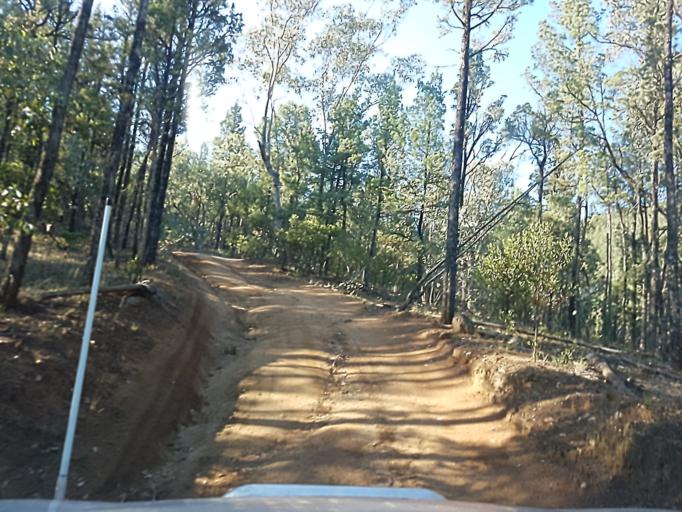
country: AU
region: New South Wales
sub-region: Snowy River
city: Jindabyne
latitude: -36.9490
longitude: 148.3801
